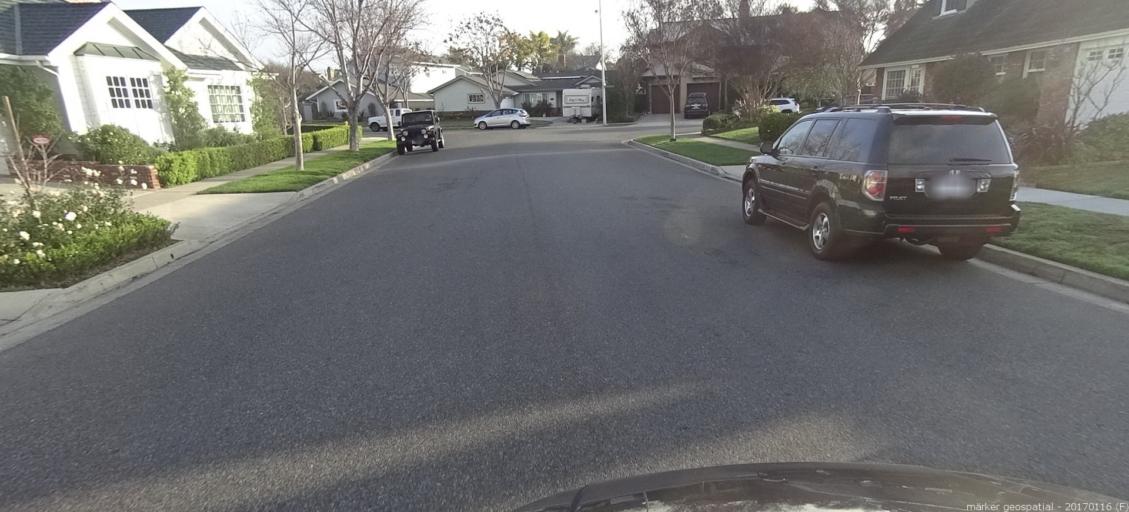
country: US
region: California
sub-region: Orange County
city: Rossmoor
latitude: 33.7912
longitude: -118.0806
